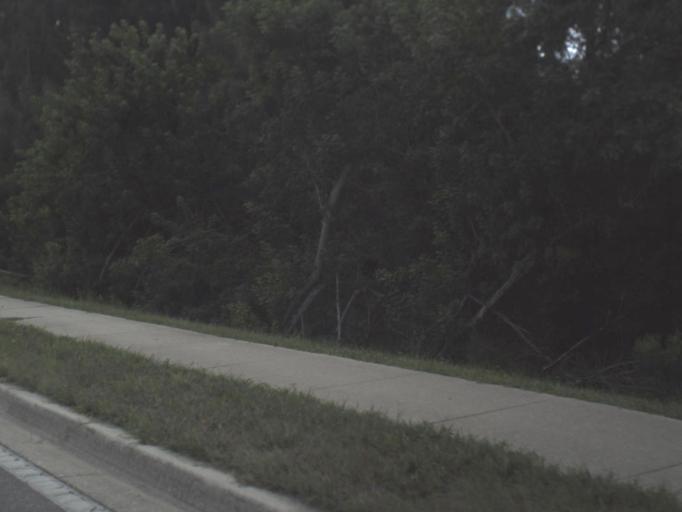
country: US
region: Florida
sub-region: Manatee County
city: Cortez
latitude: 27.4657
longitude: -82.6743
